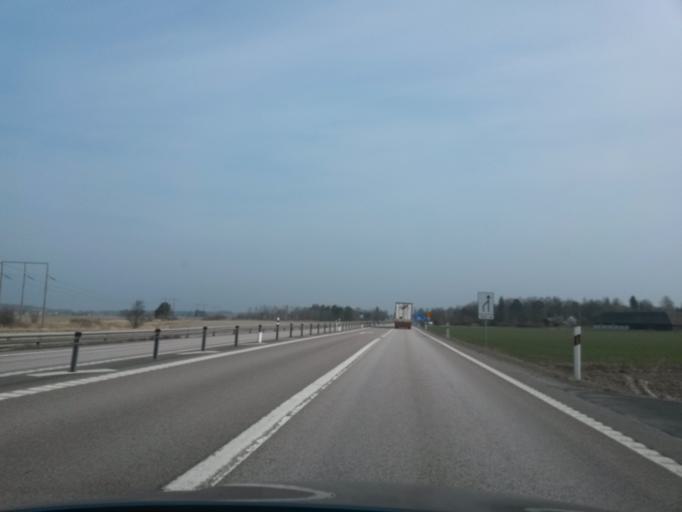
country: SE
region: Vaestra Goetaland
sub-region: Mariestads Kommun
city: Mariestad
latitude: 58.7464
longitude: 13.9494
